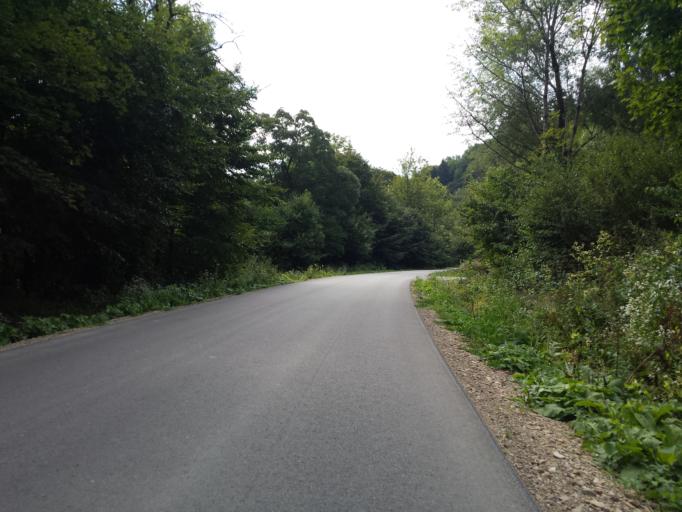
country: PL
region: Subcarpathian Voivodeship
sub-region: Powiat przemyski
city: Fredropol
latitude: 49.6271
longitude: 22.6401
